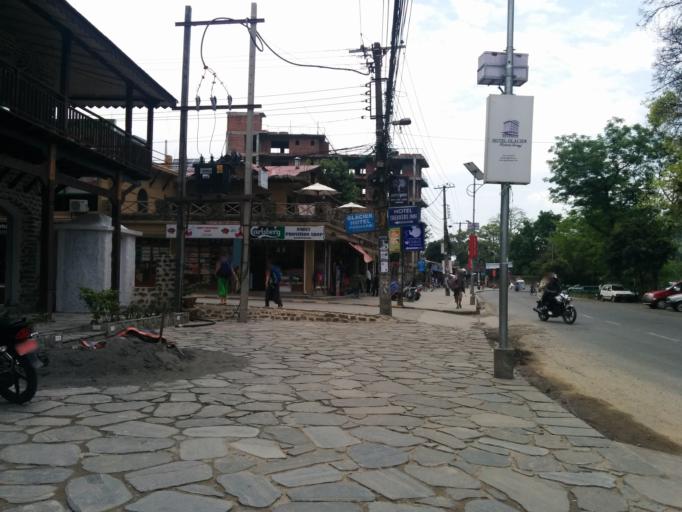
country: NP
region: Western Region
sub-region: Gandaki Zone
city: Pokhara
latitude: 28.2060
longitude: 83.9611
